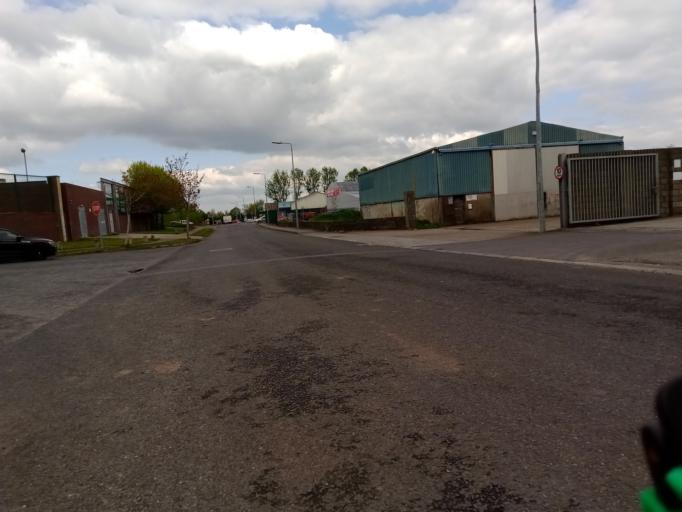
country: IE
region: Leinster
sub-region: Kilkenny
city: Kilkenny
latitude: 52.6338
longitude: -7.2429
